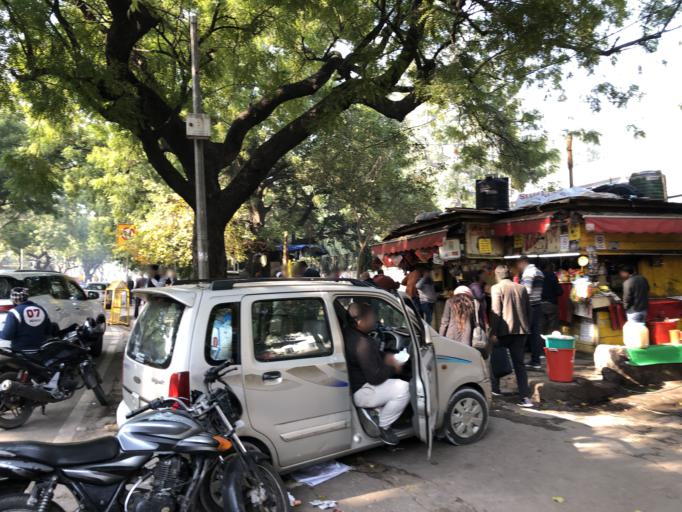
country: IN
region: NCT
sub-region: New Delhi
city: New Delhi
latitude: 28.6176
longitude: 77.2115
